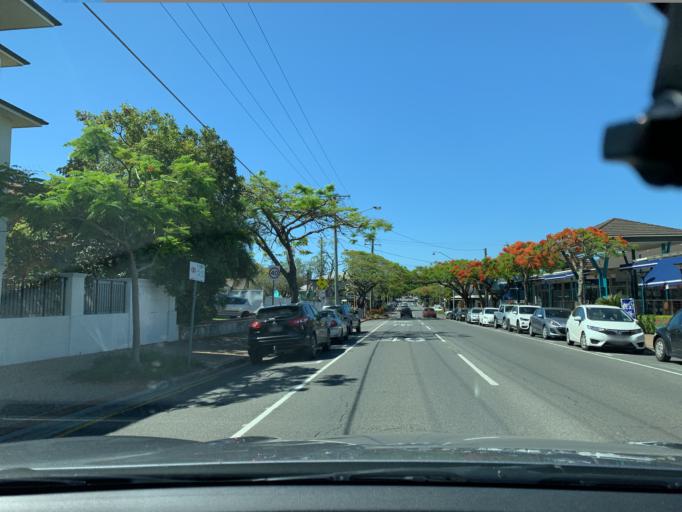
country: AU
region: Queensland
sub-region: Brisbane
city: Ascot
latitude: -27.4342
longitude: 153.0651
